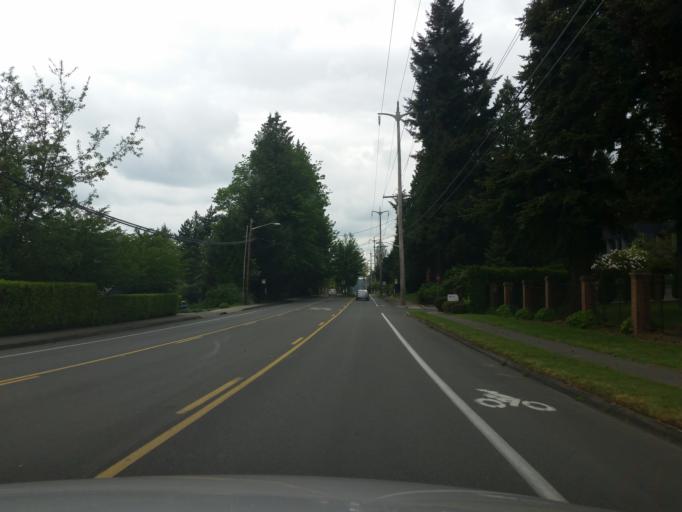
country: US
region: Washington
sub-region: King County
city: Yarrow Point
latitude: 47.6583
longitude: -122.1962
